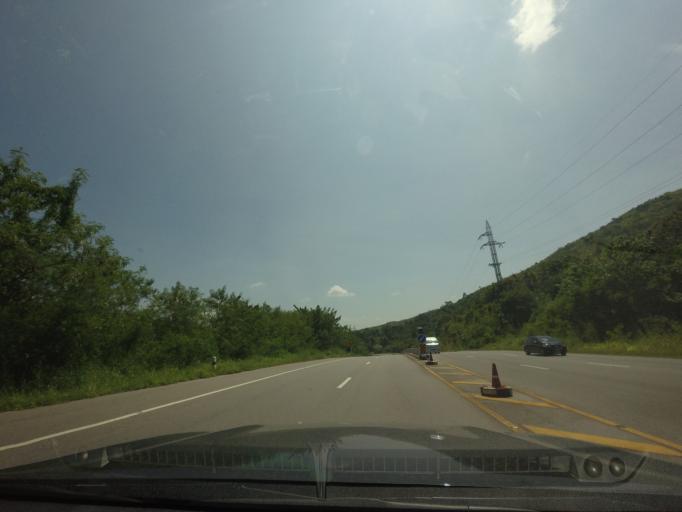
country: TH
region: Phetchabun
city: Lom Sak
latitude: 16.7694
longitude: 101.1366
